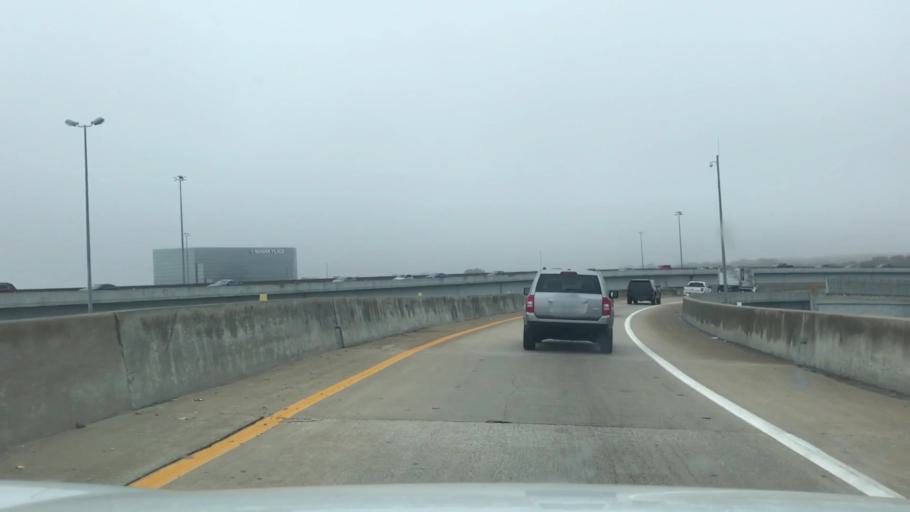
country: US
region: Missouri
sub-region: Saint Louis County
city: Brentwood
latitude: 38.6300
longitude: -90.3417
